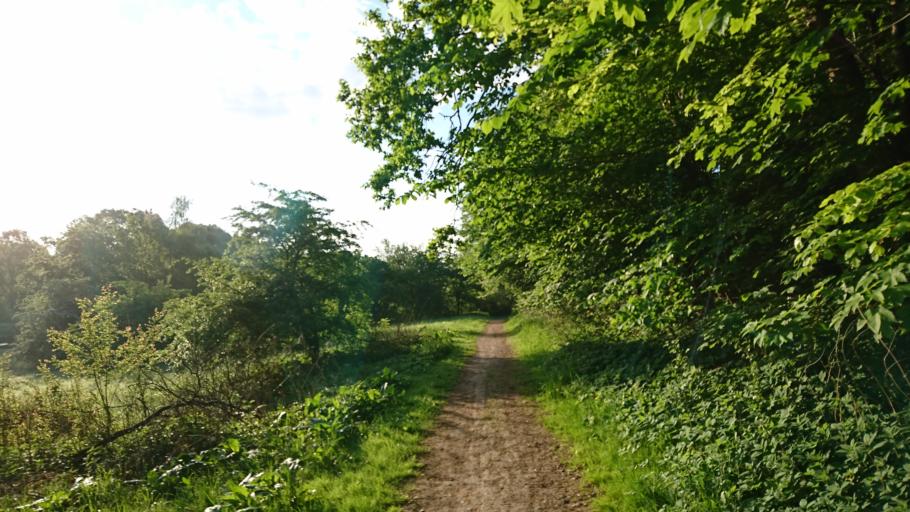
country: DK
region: Capital Region
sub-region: Ballerup Kommune
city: Ballerup
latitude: 55.7534
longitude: 12.3562
